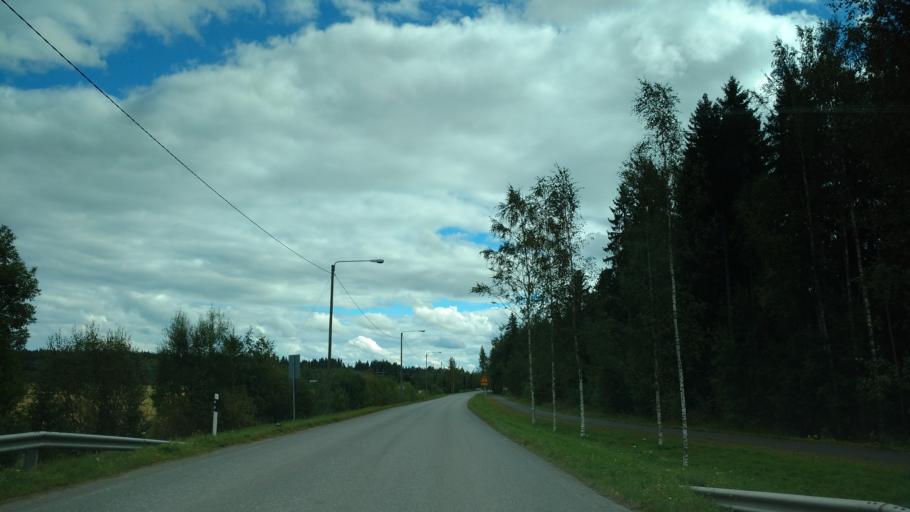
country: FI
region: Haeme
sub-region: Forssa
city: Ypaejae
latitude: 60.8105
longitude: 23.2646
